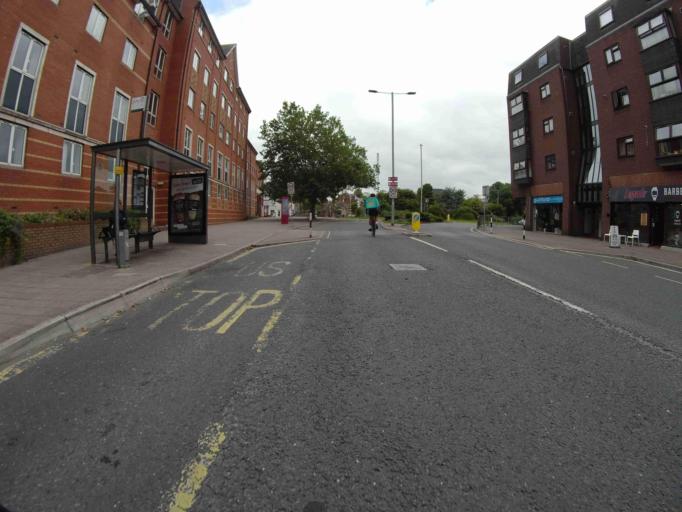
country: GB
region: England
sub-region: Devon
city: Exeter
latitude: 50.7285
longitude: -3.5217
